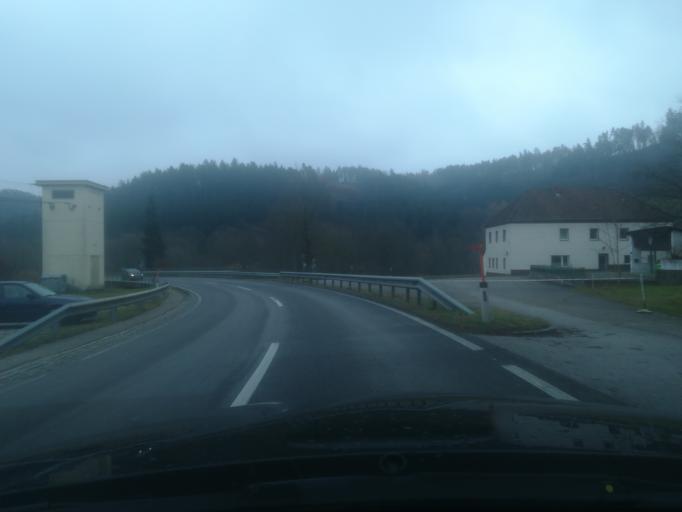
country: AT
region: Upper Austria
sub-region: Politischer Bezirk Perg
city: Perg
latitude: 48.3219
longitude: 14.5653
